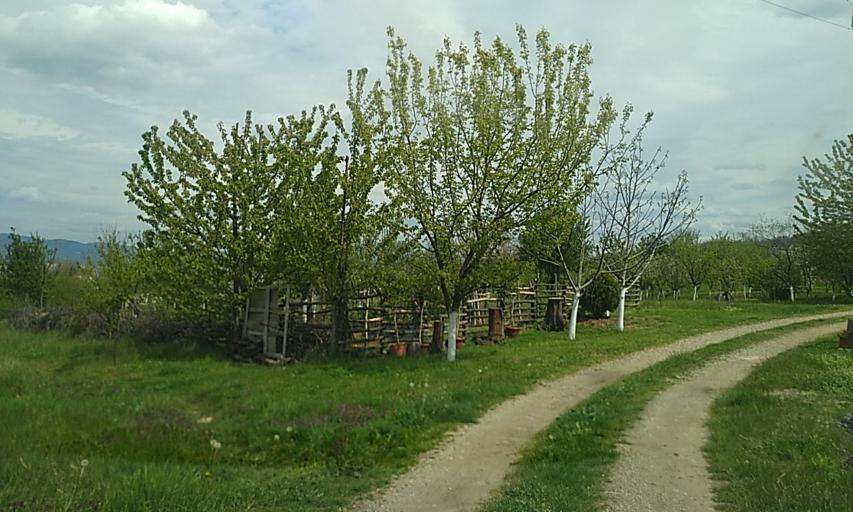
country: RS
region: Central Serbia
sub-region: Nisavski Okrug
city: Nis
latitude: 43.3096
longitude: 21.8647
